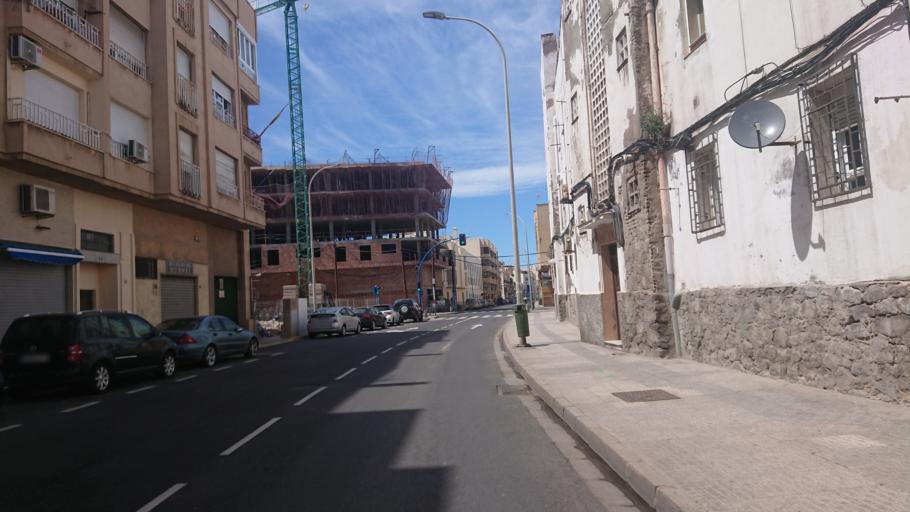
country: ES
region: Melilla
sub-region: Melilla
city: Melilla
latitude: 35.2816
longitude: -2.9406
